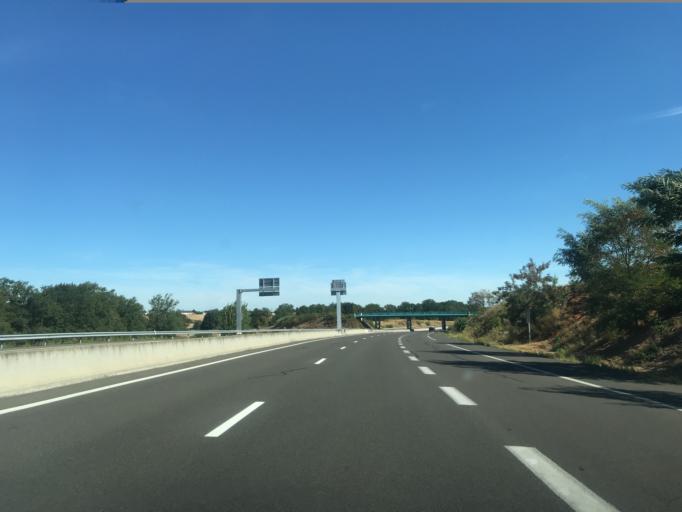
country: FR
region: Auvergne
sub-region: Departement de l'Allier
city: Premilhat
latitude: 46.3354
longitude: 2.5360
